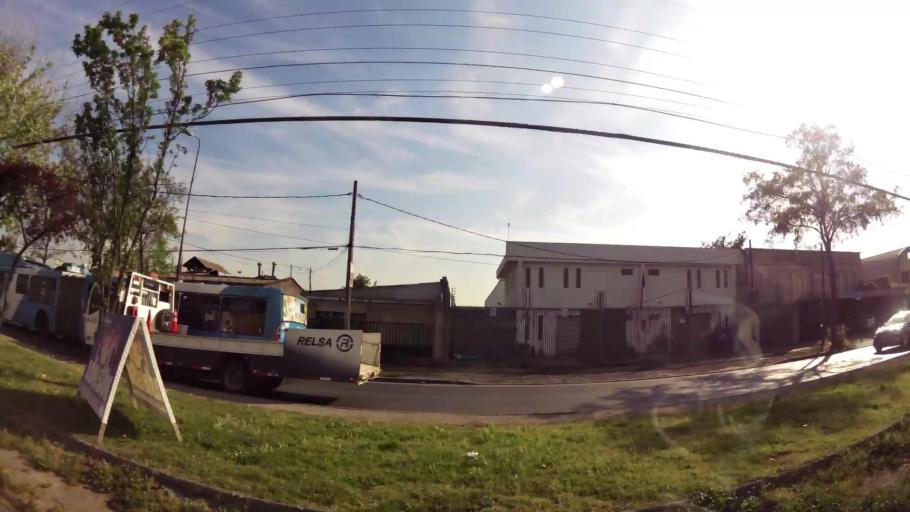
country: CL
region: Santiago Metropolitan
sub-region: Provincia de Santiago
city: Santiago
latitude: -33.5054
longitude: -70.6467
